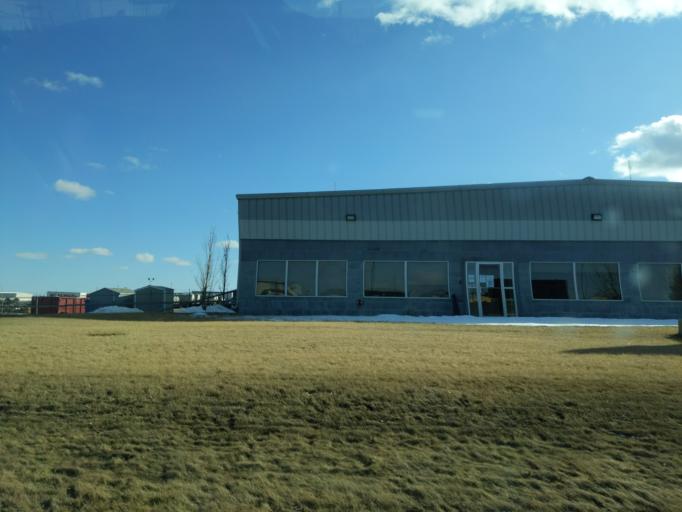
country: CA
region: Saskatchewan
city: Lloydminster
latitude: 53.2998
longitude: -110.0405
